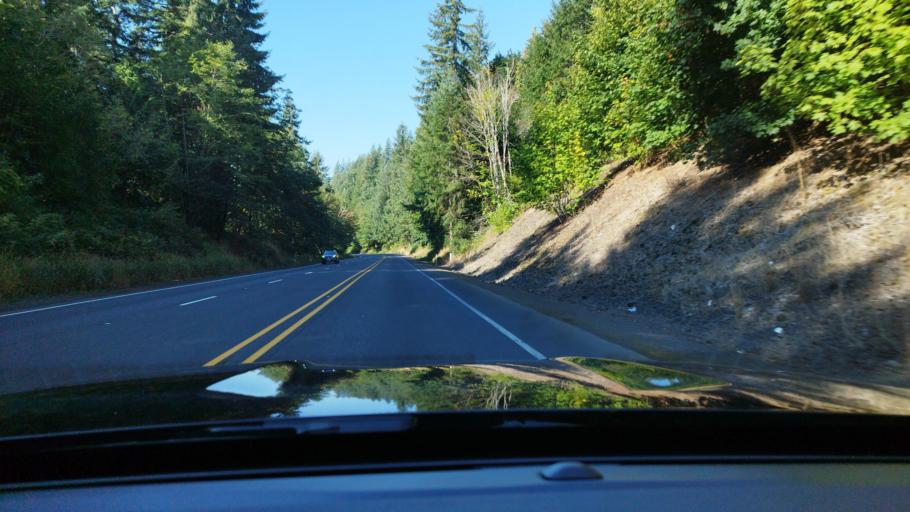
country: US
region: Oregon
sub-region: Columbia County
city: Clatskanie
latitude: 46.1034
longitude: -123.1689
